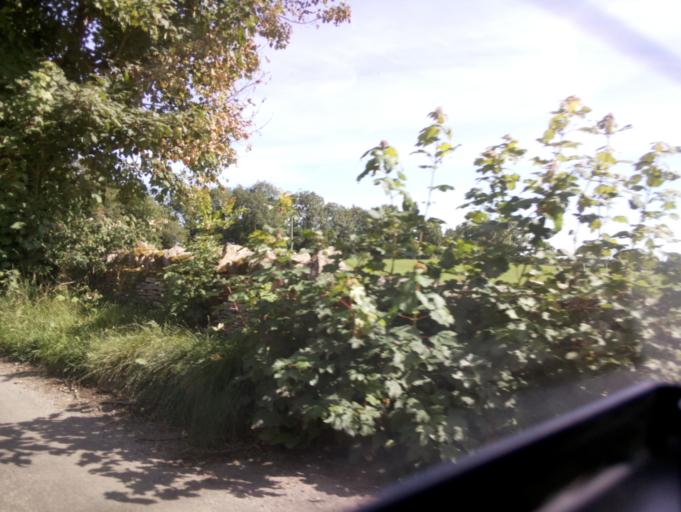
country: GB
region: England
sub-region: Wiltshire
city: Nettleton
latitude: 51.4986
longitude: -2.2570
